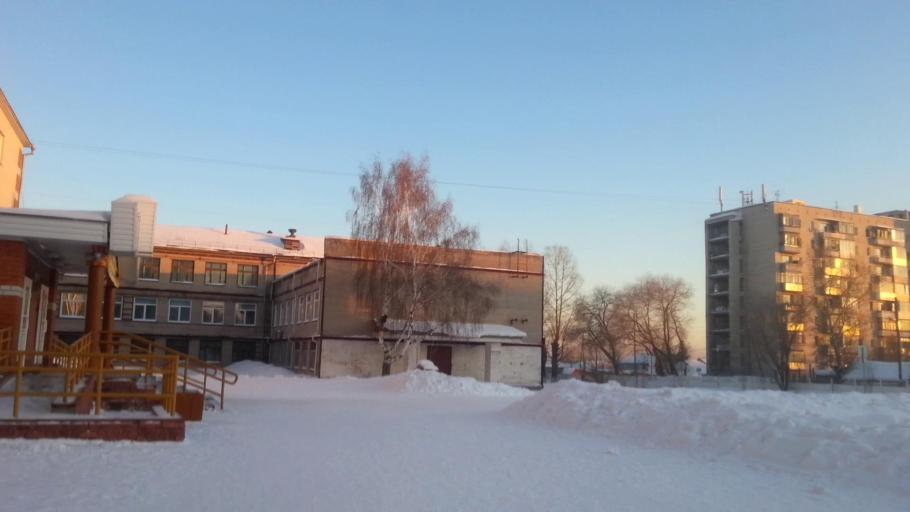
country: RU
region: Altai Krai
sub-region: Gorod Barnaulskiy
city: Barnaul
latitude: 53.3541
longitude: 83.7045
